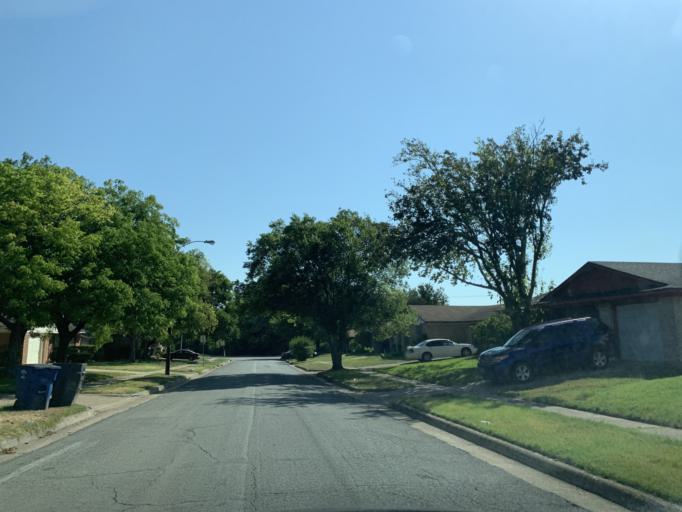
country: US
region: Texas
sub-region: Dallas County
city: Hutchins
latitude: 32.6680
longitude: -96.7612
